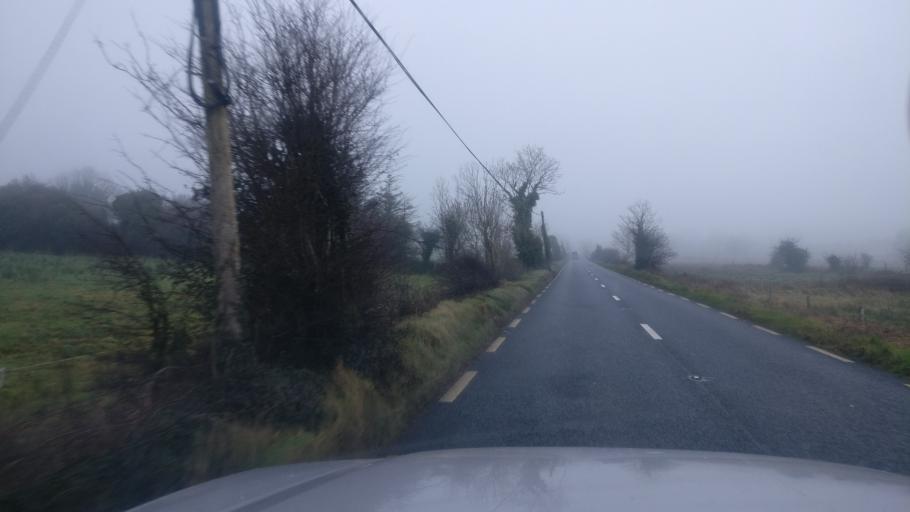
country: IE
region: Connaught
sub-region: County Galway
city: Loughrea
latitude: 53.1863
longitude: -8.6235
